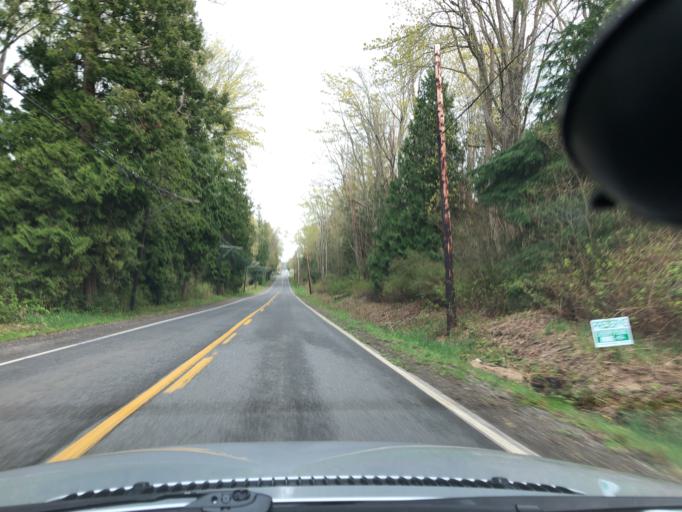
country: US
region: Washington
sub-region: Whatcom County
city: Birch Bay
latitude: 48.8925
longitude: -122.7763
